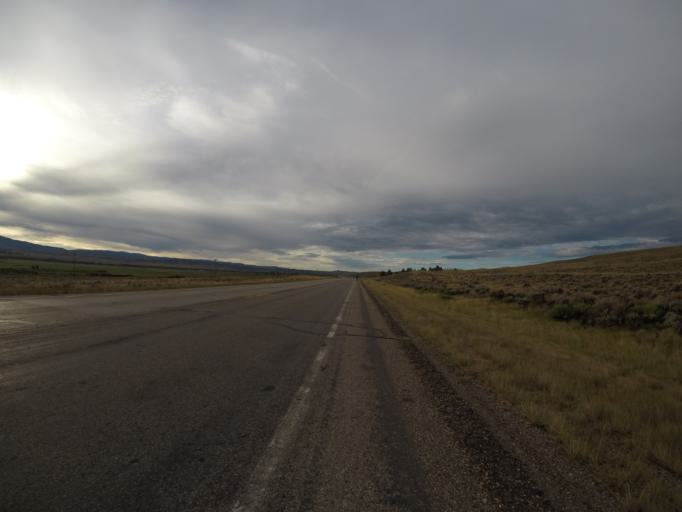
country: US
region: Wyoming
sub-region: Carbon County
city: Saratoga
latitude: 41.4015
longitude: -106.7710
